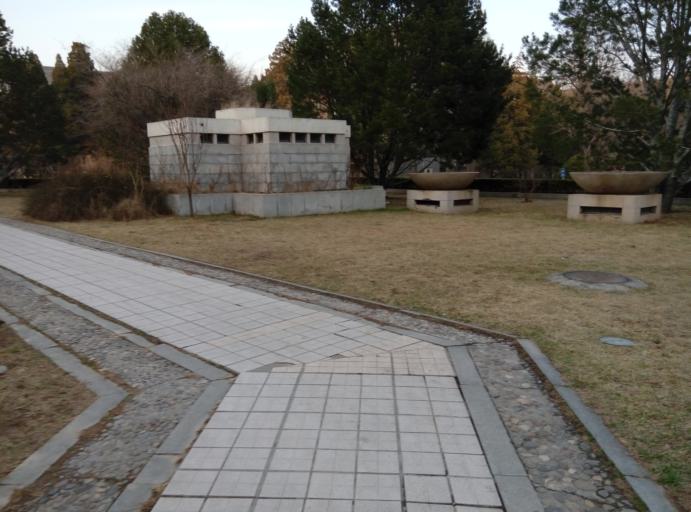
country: CN
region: Beijing
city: Haidian
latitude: 39.9908
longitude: 116.3047
